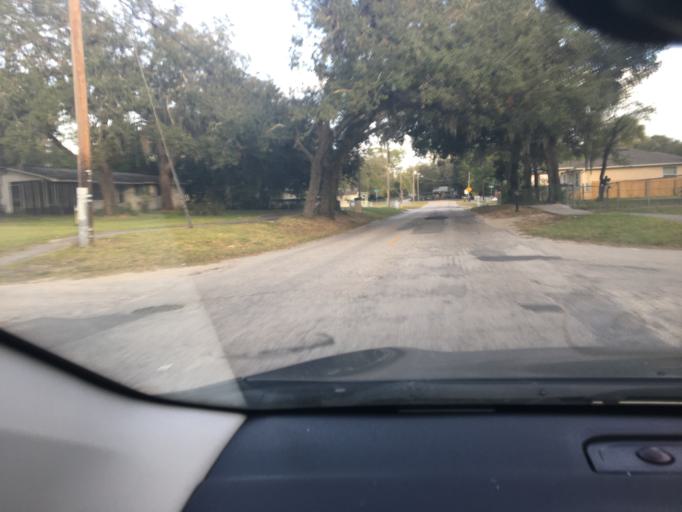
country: US
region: Florida
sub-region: Hillsborough County
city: University
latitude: 28.0399
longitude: -82.4417
